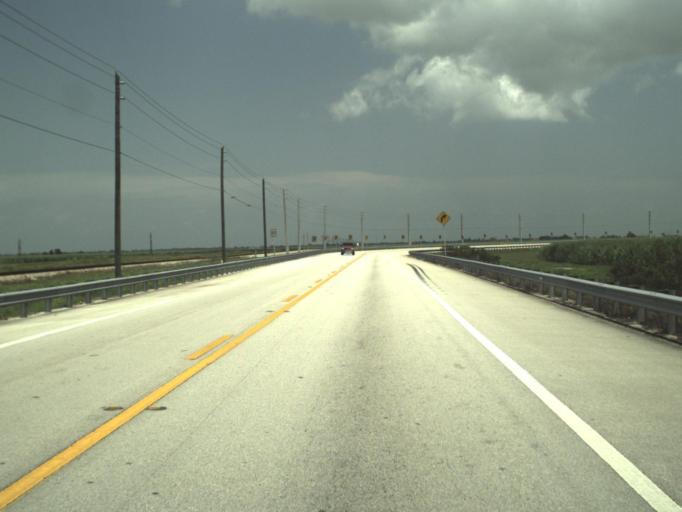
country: US
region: Florida
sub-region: Palm Beach County
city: Pahokee
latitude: 26.7661
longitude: -80.6597
